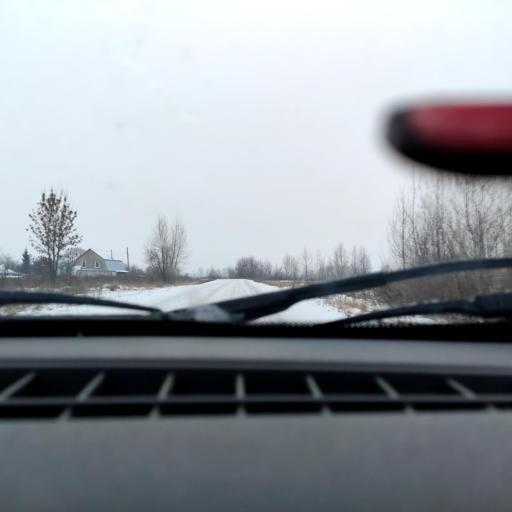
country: RU
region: Bashkortostan
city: Blagoveshchensk
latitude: 54.9042
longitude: 56.0130
